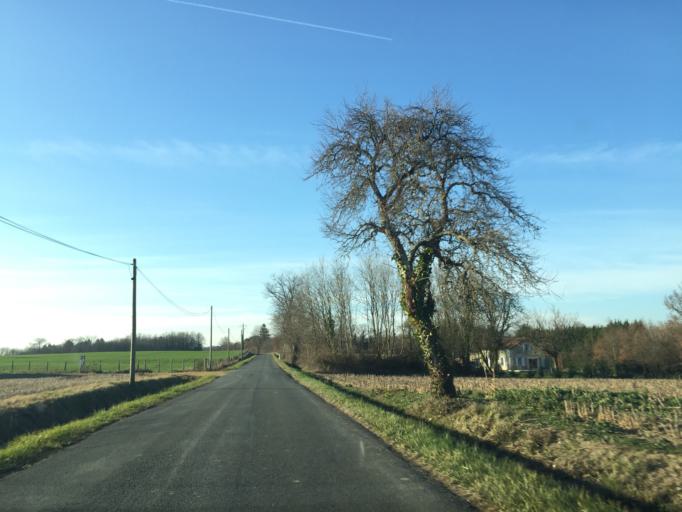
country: FR
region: Aquitaine
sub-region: Departement de la Dordogne
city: Riberac
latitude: 45.2014
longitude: 0.3263
